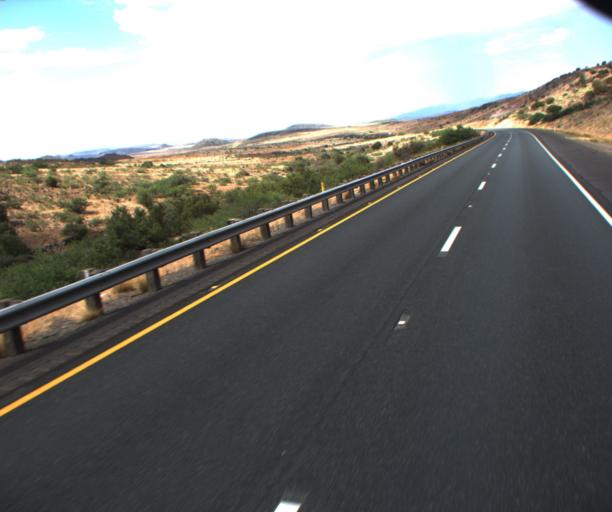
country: US
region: Arizona
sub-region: Yavapai County
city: Cordes Lakes
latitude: 34.4610
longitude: -112.0311
